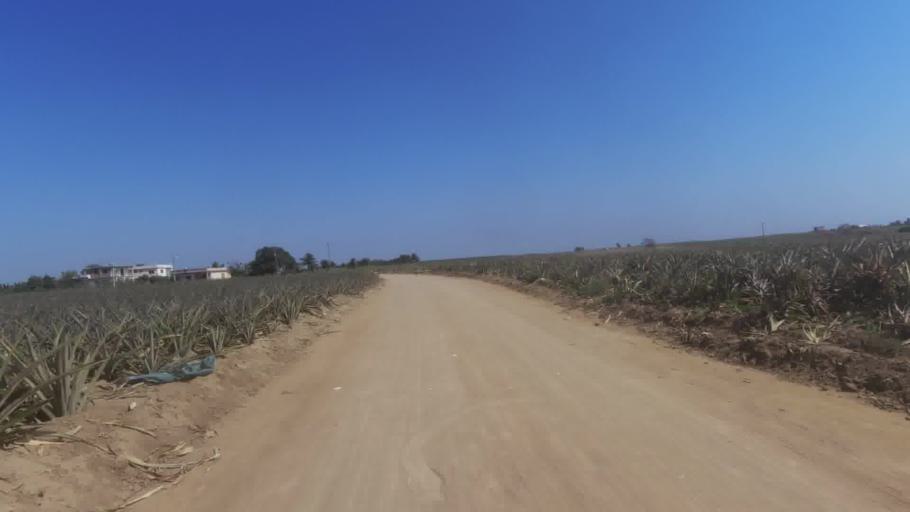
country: BR
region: Espirito Santo
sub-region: Marataizes
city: Marataizes
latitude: -21.1056
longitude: -40.8609
